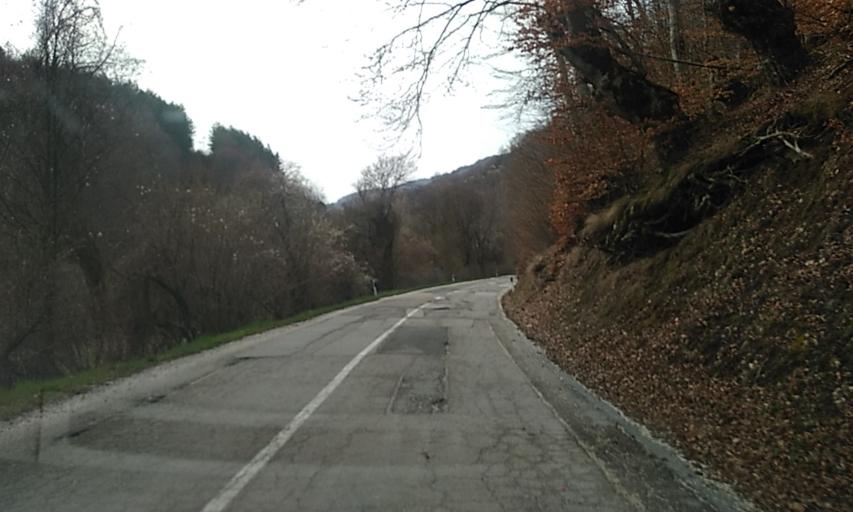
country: RS
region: Central Serbia
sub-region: Pcinjski Okrug
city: Bosilegrad
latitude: 42.5474
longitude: 22.3962
